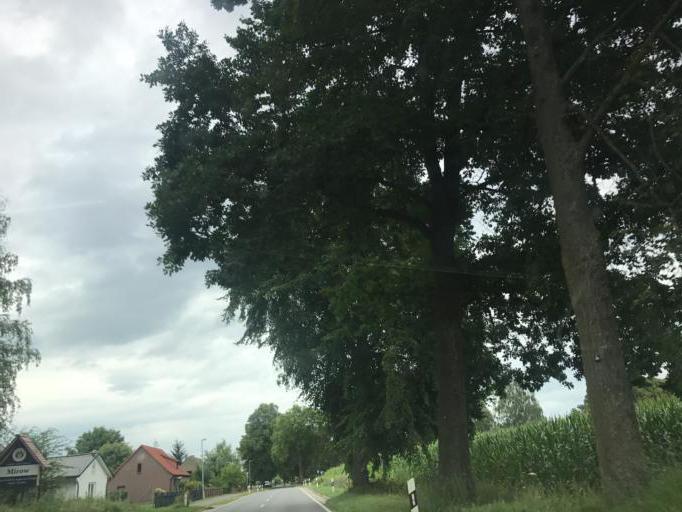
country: DE
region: Mecklenburg-Vorpommern
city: Rechlin
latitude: 53.2697
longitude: 12.7976
